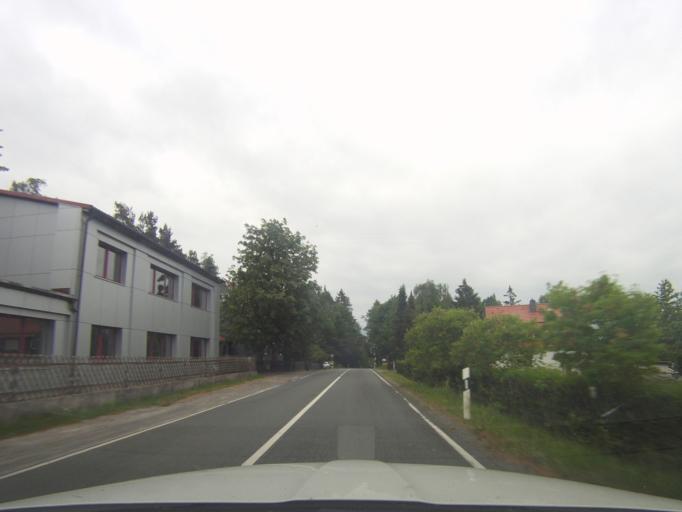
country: DE
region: Thuringia
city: Schleusingen
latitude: 50.4874
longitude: 10.8365
